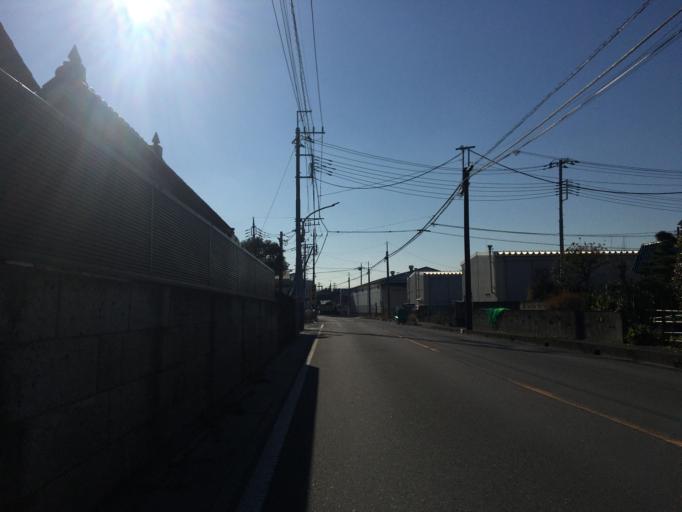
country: JP
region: Saitama
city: Soka
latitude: 35.8007
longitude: 139.8220
